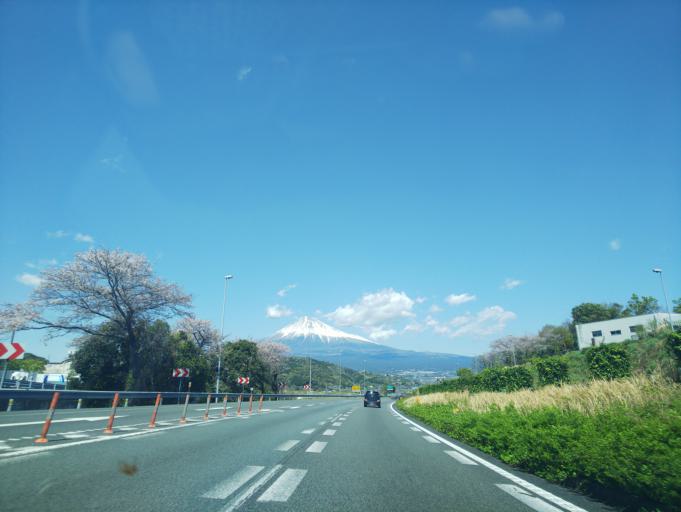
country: JP
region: Shizuoka
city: Fujinomiya
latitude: 35.1592
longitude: 138.6186
